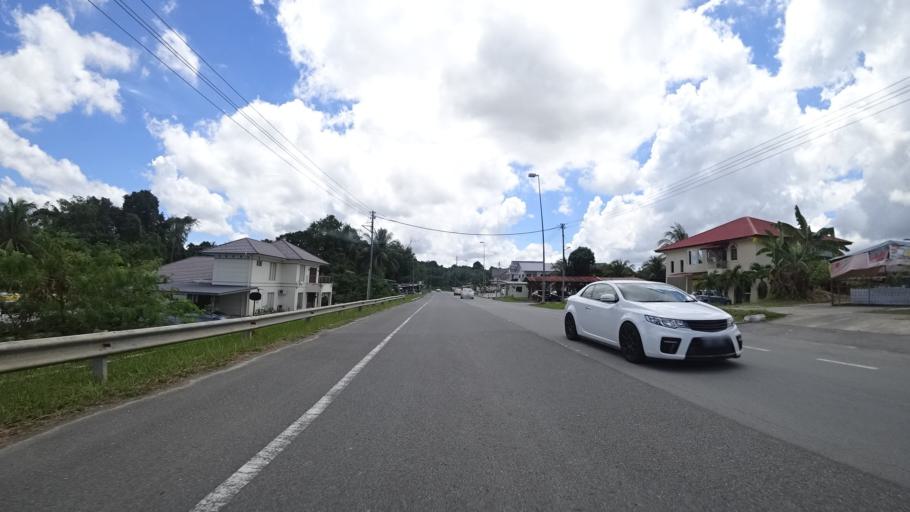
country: BN
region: Brunei and Muara
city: Bandar Seri Begawan
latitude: 4.9370
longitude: 114.9557
